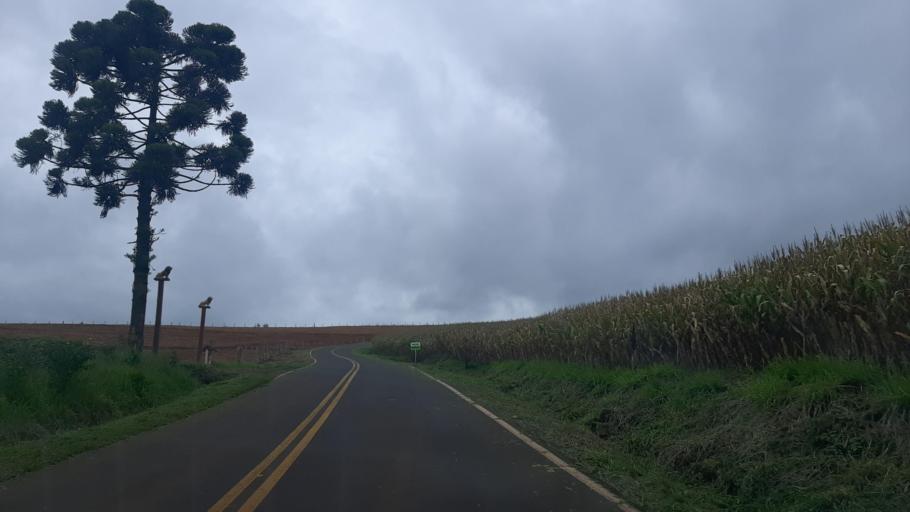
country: BR
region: Parana
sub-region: Ampere
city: Ampere
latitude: -25.9467
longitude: -53.4594
